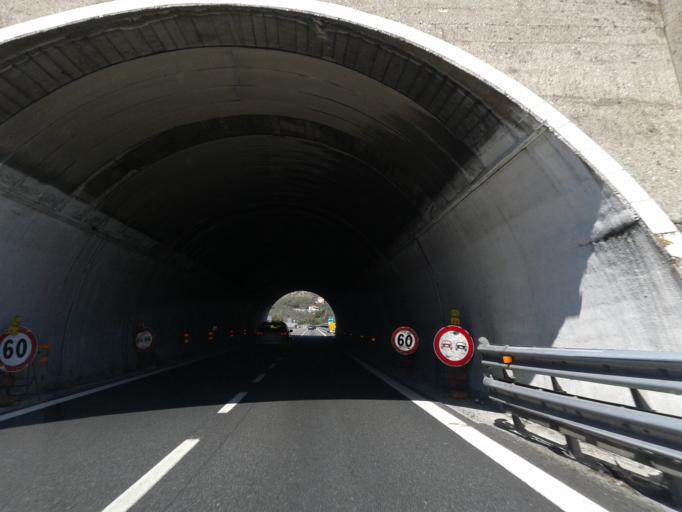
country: IT
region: Liguria
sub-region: Provincia di Genova
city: Sestri Levante
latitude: 44.2795
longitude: 9.4152
